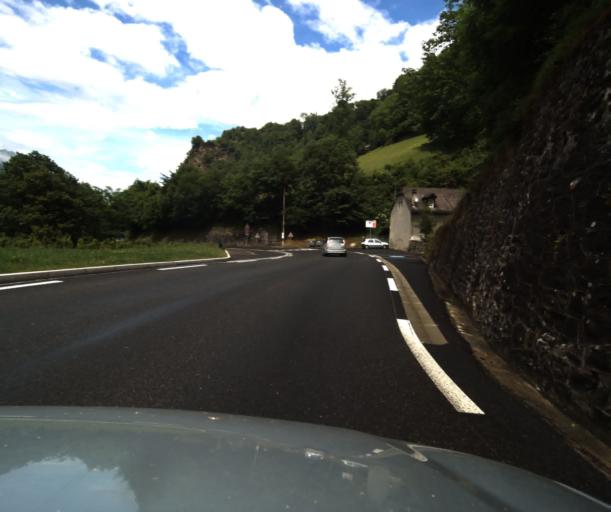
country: FR
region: Midi-Pyrenees
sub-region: Departement des Hautes-Pyrenees
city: Luz-Saint-Sauveur
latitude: 42.8595
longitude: -0.0050
